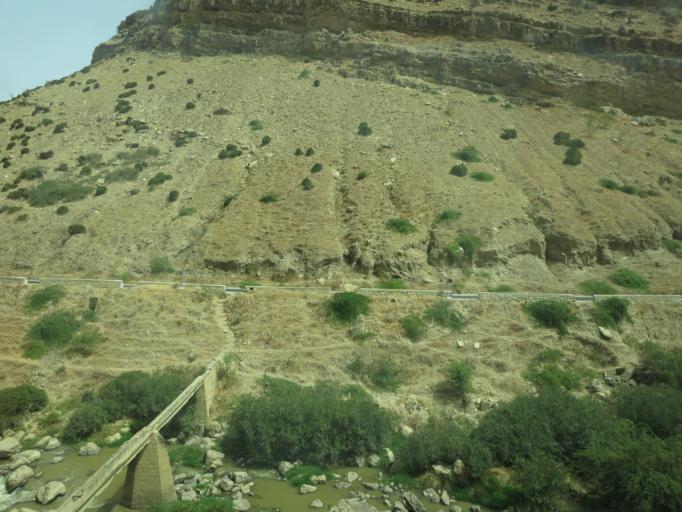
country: MA
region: Gharb-Chrarda-Beni Hssen
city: Sidi Qacem
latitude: 34.1837
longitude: -5.7074
